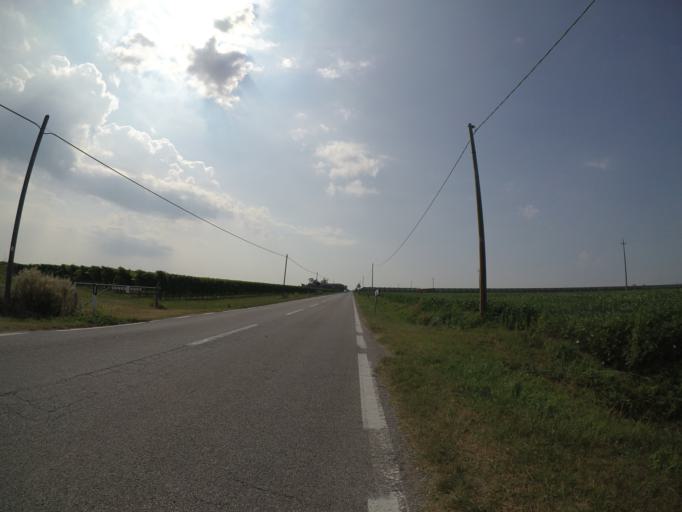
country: IT
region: Friuli Venezia Giulia
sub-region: Provincia di Udine
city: Pertegada
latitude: 45.7524
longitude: 13.0589
